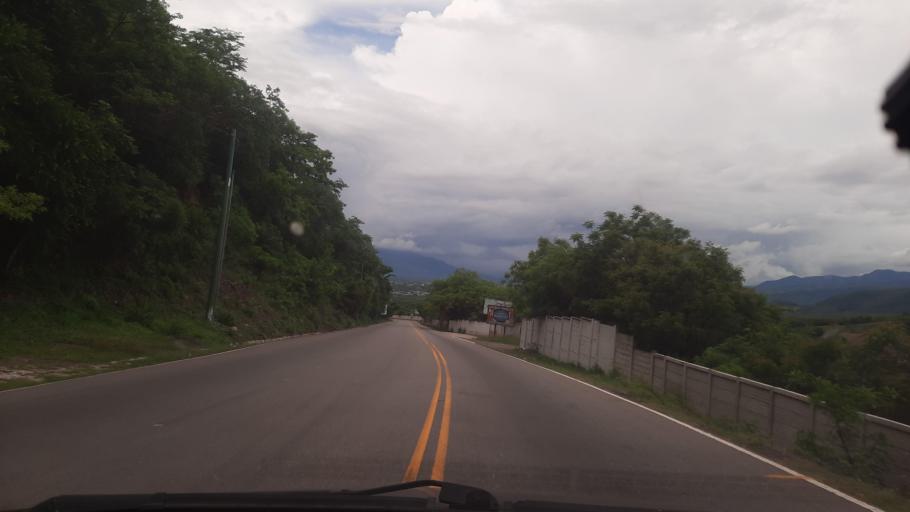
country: GT
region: Chiquimula
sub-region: Municipio de Chiquimula
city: Chiquimula
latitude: 14.8570
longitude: -89.5185
